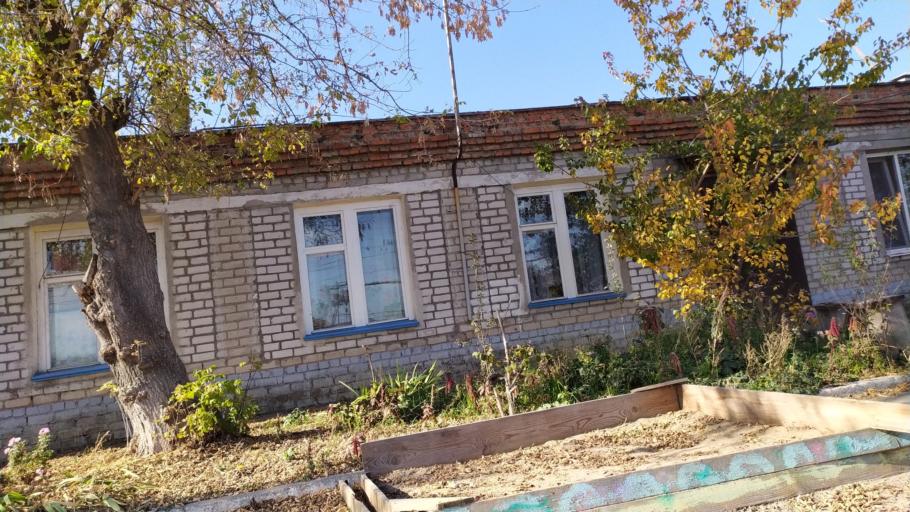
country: RU
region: Kursk
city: Kursk
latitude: 51.6536
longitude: 36.1537
